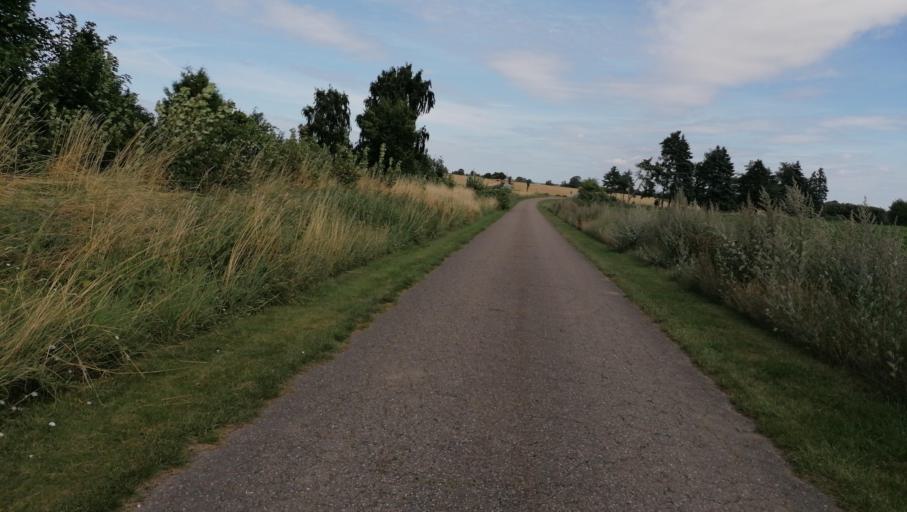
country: DK
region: Zealand
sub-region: Odsherred Kommune
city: Horve
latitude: 55.7577
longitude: 11.4594
